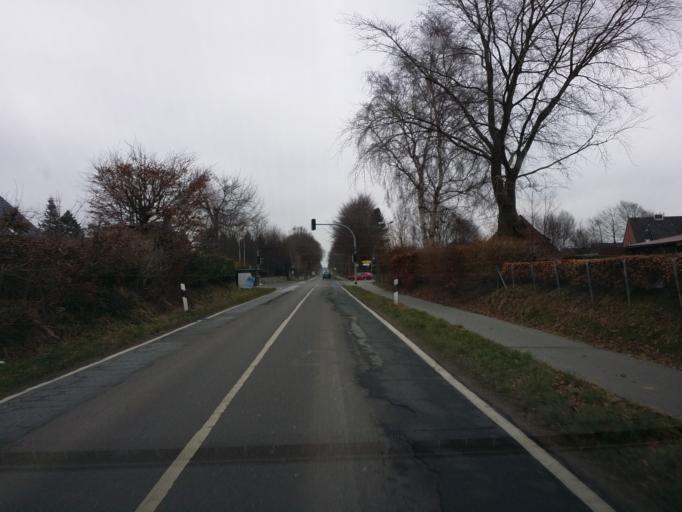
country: DE
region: Schleswig-Holstein
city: Schacht-Audorf
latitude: 54.3142
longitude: 9.7275
